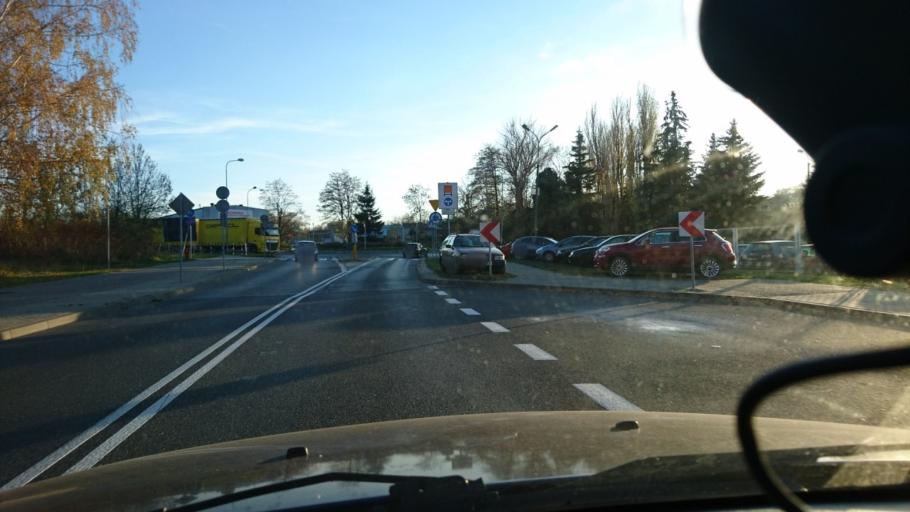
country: PL
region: Silesian Voivodeship
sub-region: Bielsko-Biala
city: Bielsko-Biala
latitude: 49.8415
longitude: 19.0466
